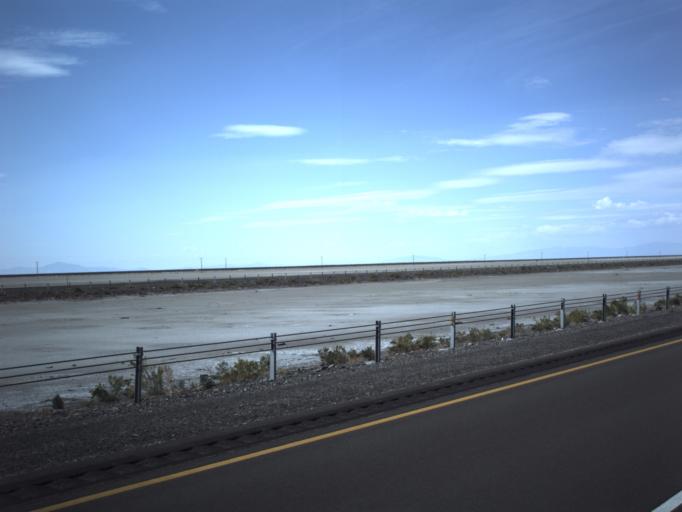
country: US
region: Utah
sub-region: Tooele County
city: Wendover
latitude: 40.7288
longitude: -113.3648
